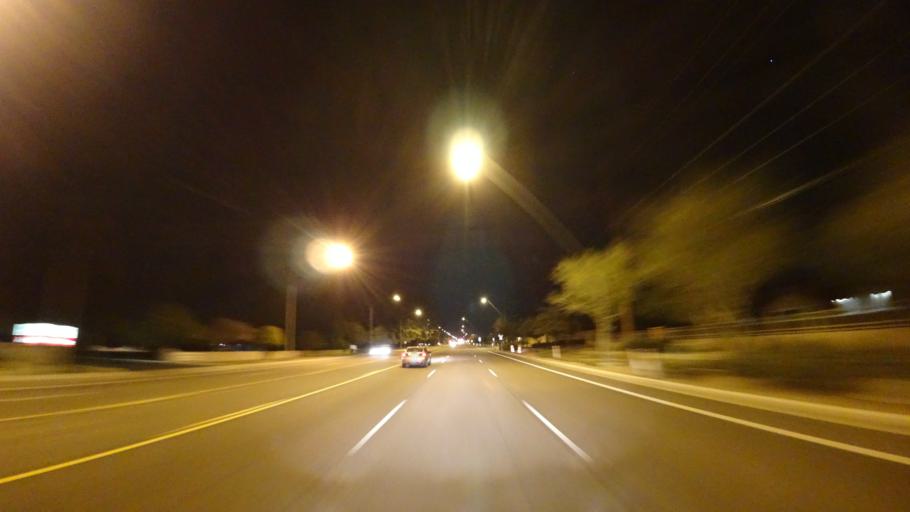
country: US
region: Arizona
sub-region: Maricopa County
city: Gilbert
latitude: 33.3935
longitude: -111.7777
